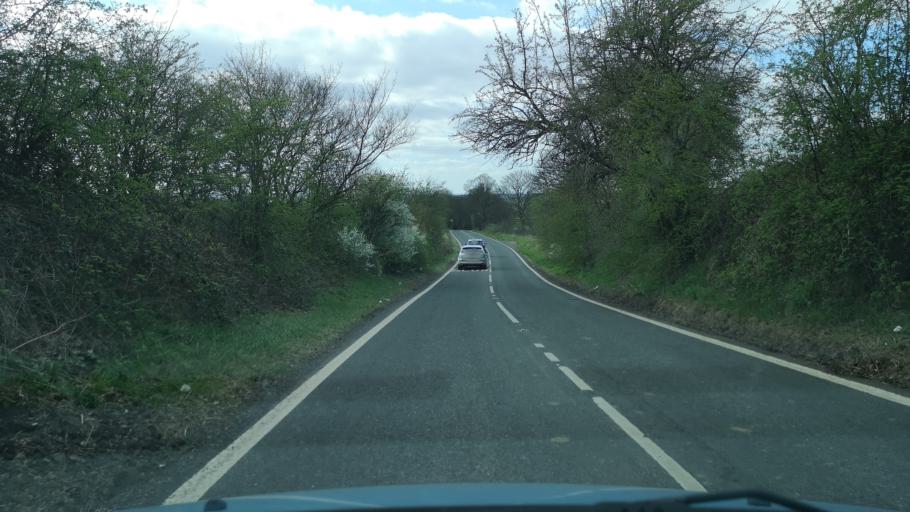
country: GB
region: England
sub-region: City and Borough of Wakefield
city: Crofton
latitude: 53.6733
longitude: -1.4356
